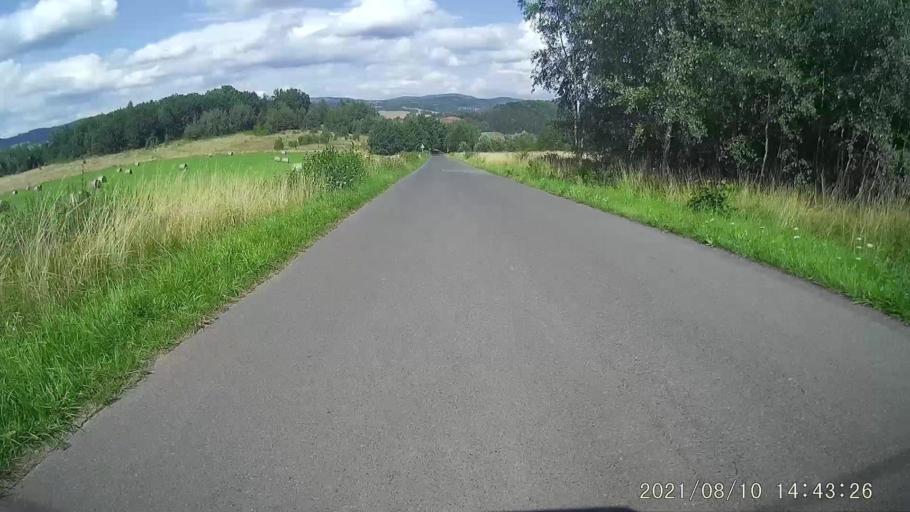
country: PL
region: Lower Silesian Voivodeship
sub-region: Powiat klodzki
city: Radkow
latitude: 50.5468
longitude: 16.4288
